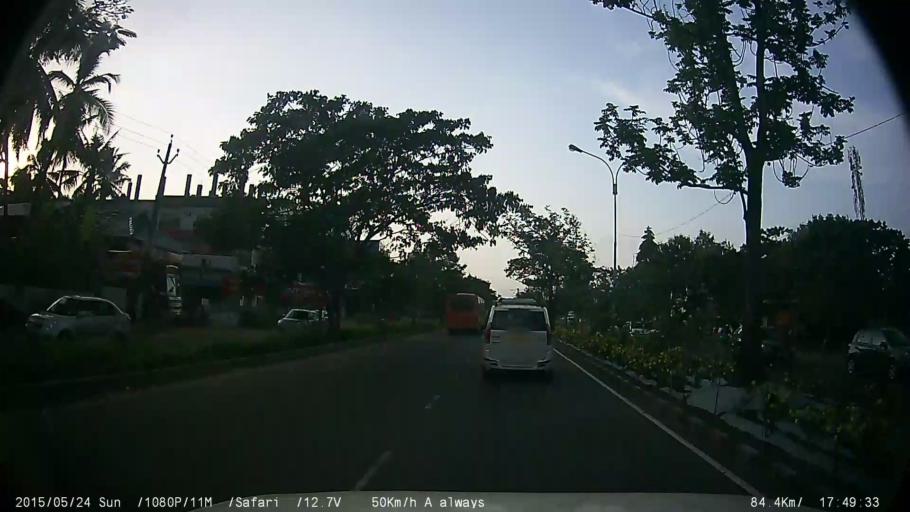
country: IN
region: Kerala
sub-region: Ernakulam
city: Cochin
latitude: 9.9909
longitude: 76.3153
